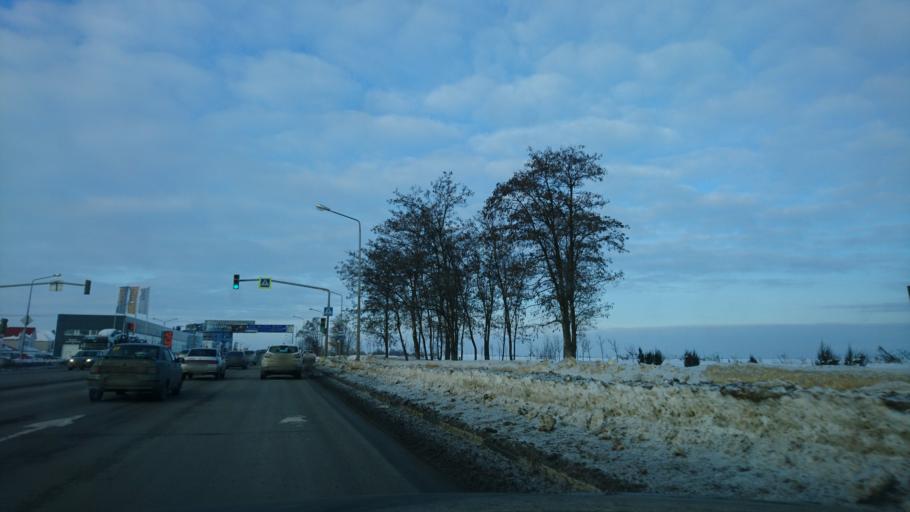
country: RU
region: Belgorod
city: Severnyy
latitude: 50.6516
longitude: 36.5664
